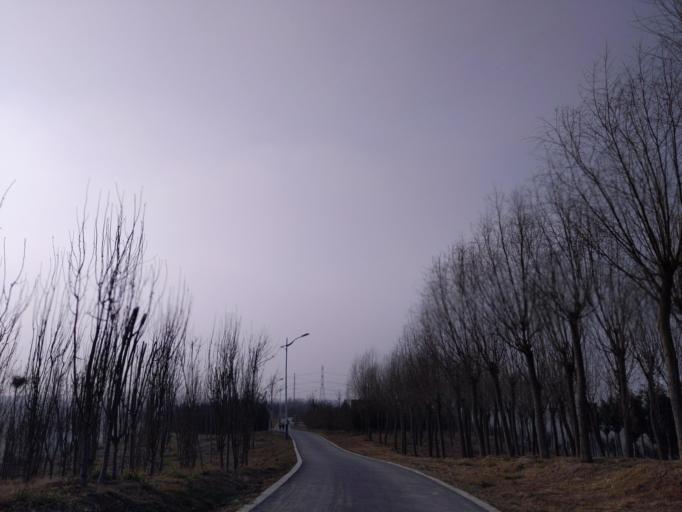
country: CN
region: Henan Sheng
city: Puyang
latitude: 35.8199
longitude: 115.0056
